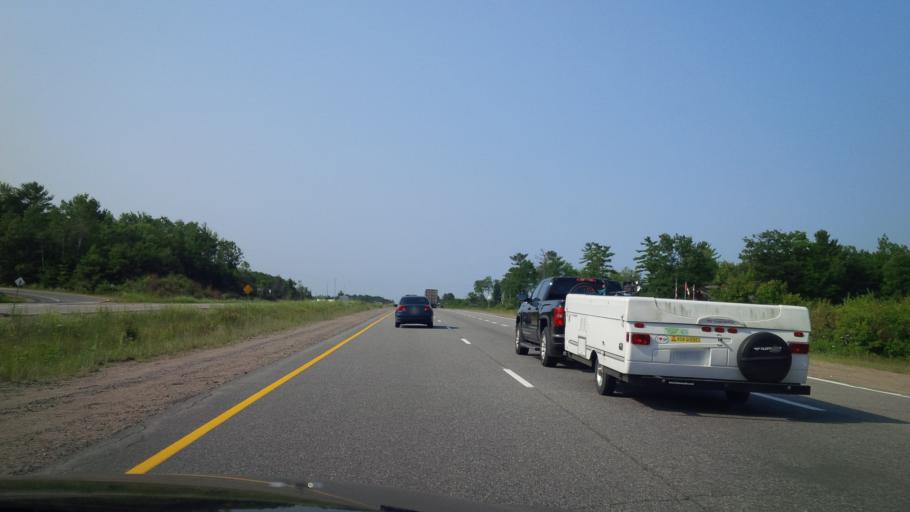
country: CA
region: Ontario
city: Bracebridge
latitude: 44.9953
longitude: -79.3064
